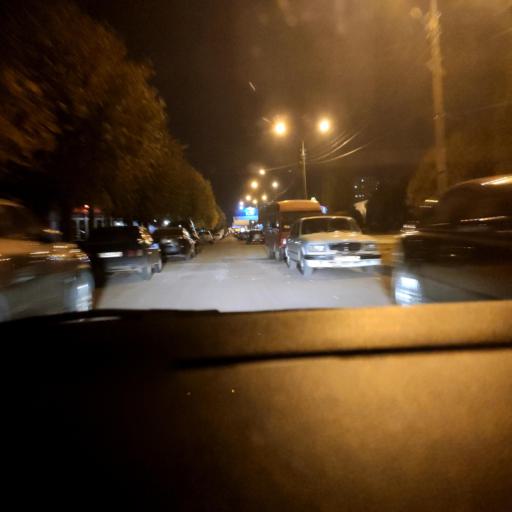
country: RU
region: Voronezj
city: Voronezh
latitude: 51.7066
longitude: 39.1778
